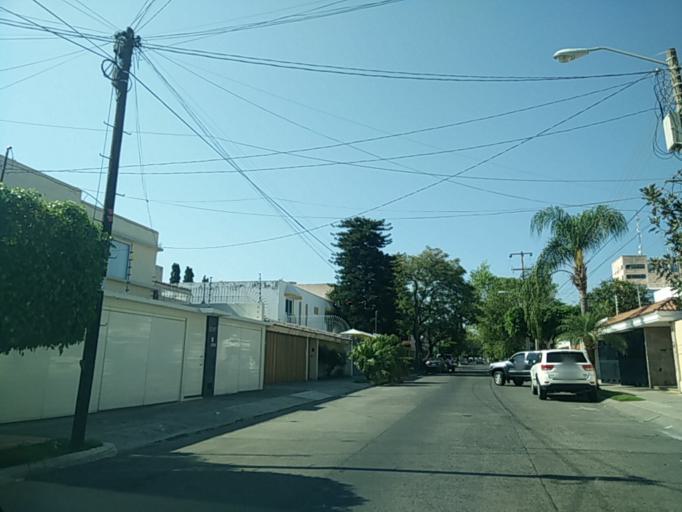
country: MX
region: Jalisco
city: Guadalajara
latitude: 20.6517
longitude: -103.3953
